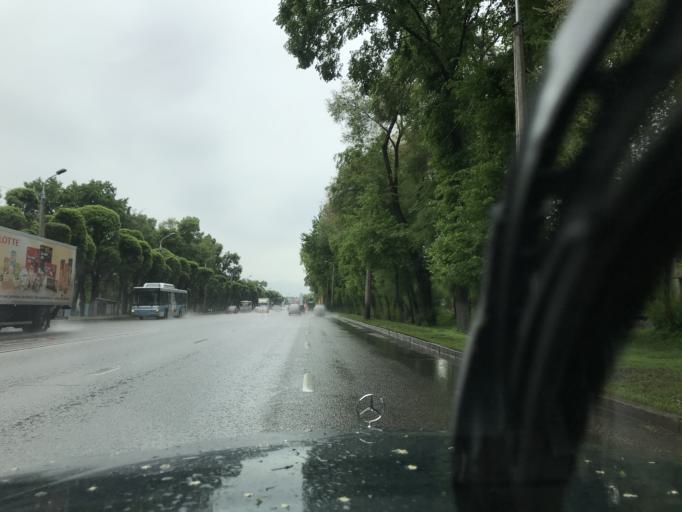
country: KZ
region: Almaty Qalasy
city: Almaty
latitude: 43.3024
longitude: 76.9523
